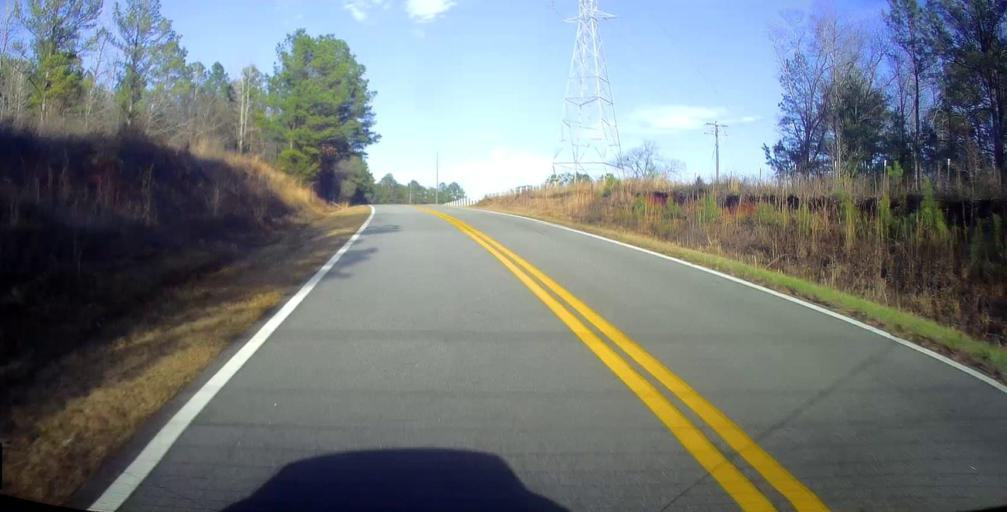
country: US
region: Georgia
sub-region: Bibb County
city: West Point
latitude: 32.8377
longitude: -83.9166
